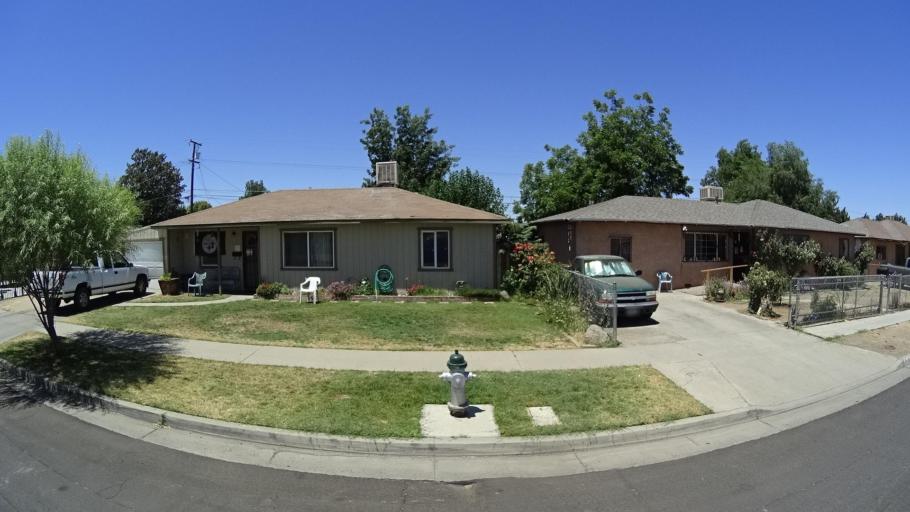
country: US
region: California
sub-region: Fresno County
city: Fresno
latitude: 36.7121
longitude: -119.7538
